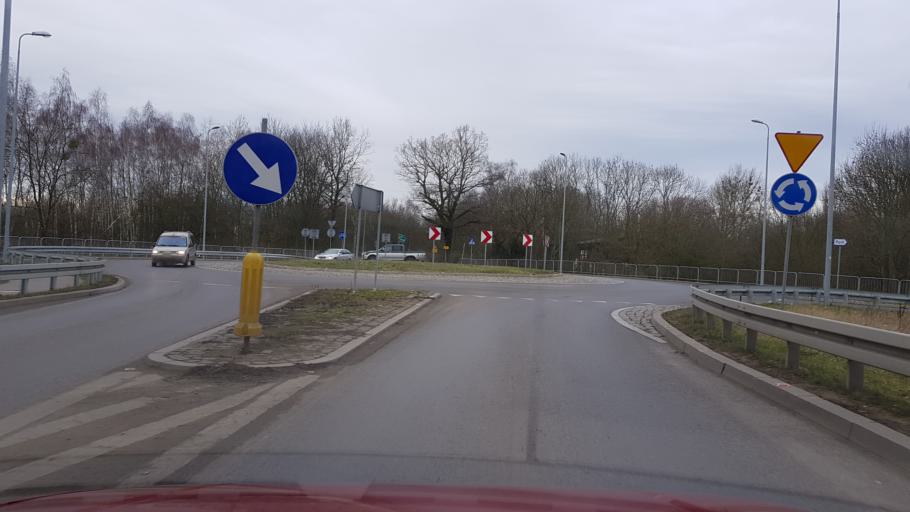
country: PL
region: West Pomeranian Voivodeship
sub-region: Powiat policki
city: Police
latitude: 53.5587
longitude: 14.5660
